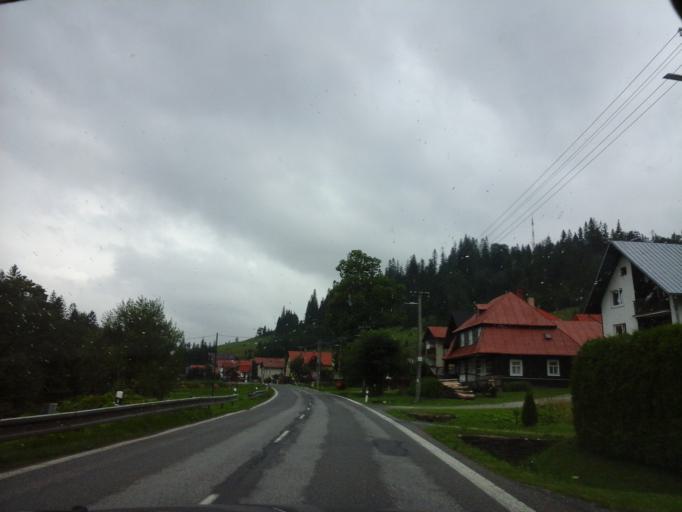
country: SK
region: Presovsky
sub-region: Okres Poprad
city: Zdiar
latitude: 49.2659
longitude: 20.2940
